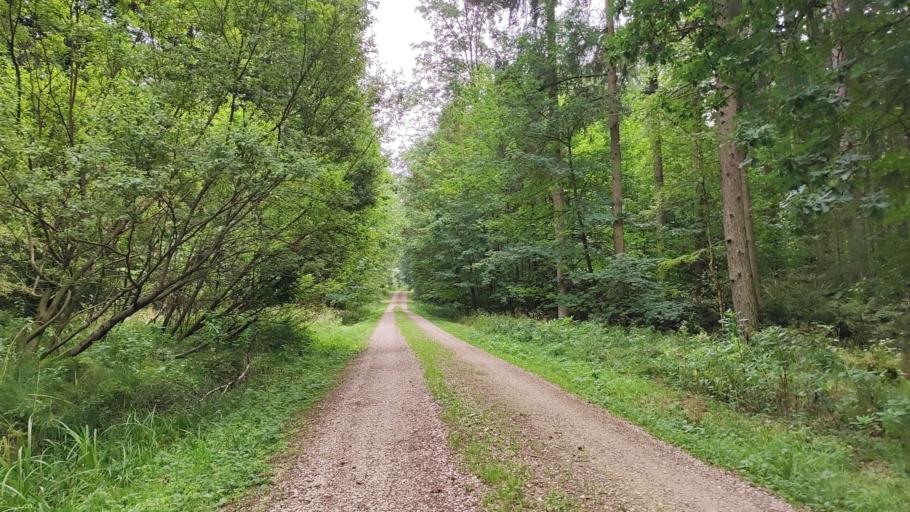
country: DE
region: Bavaria
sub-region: Swabia
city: Landensberg
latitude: 48.4279
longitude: 10.5157
